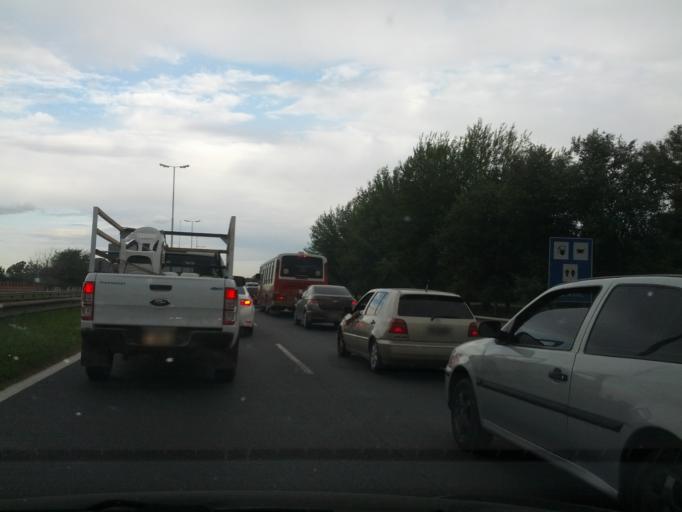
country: AR
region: Buenos Aires
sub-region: Partido de General Rodriguez
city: General Rodriguez
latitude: -34.5807
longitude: -59.0049
